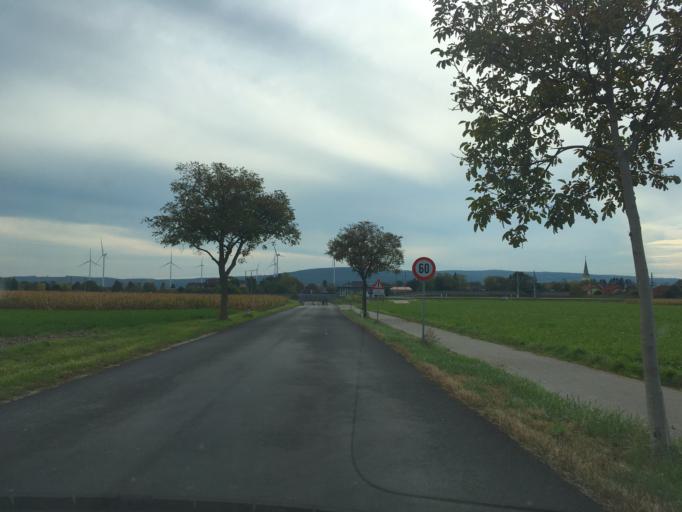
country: AT
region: Lower Austria
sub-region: Politischer Bezirk Bruck an der Leitha
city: Trautmannsdorf an der Leitha
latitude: 48.0254
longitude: 16.6776
